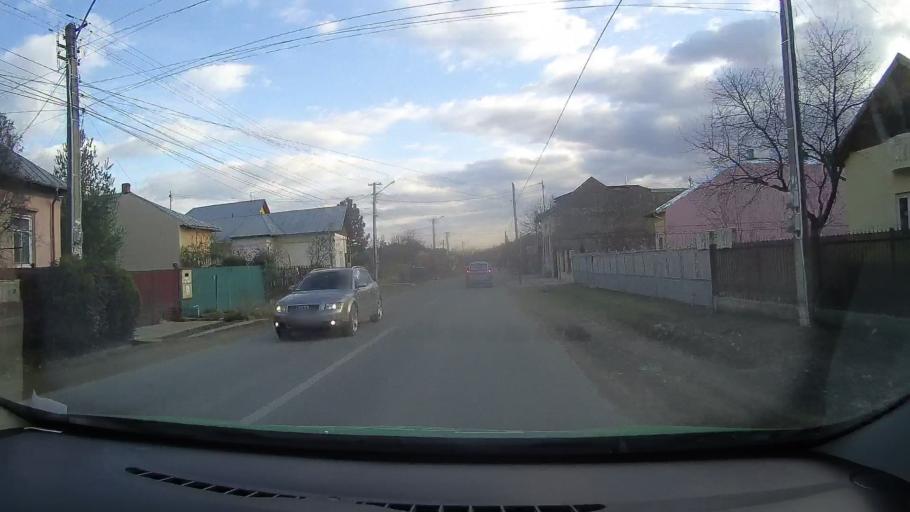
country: RO
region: Dambovita
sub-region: Comuna Gura Ocnitei
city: Gura Ocnitei
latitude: 44.9480
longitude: 25.5591
